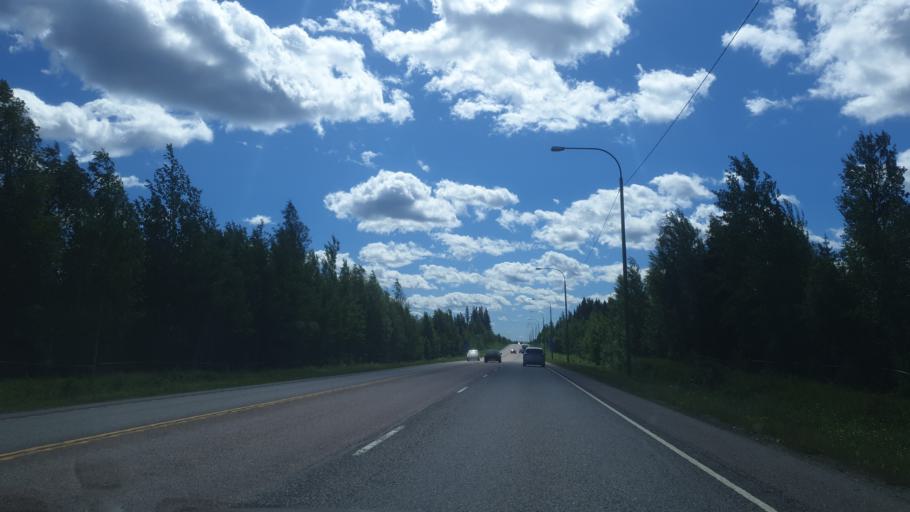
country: FI
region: Northern Savo
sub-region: Varkaus
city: Varkaus
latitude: 62.3764
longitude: 27.8095
